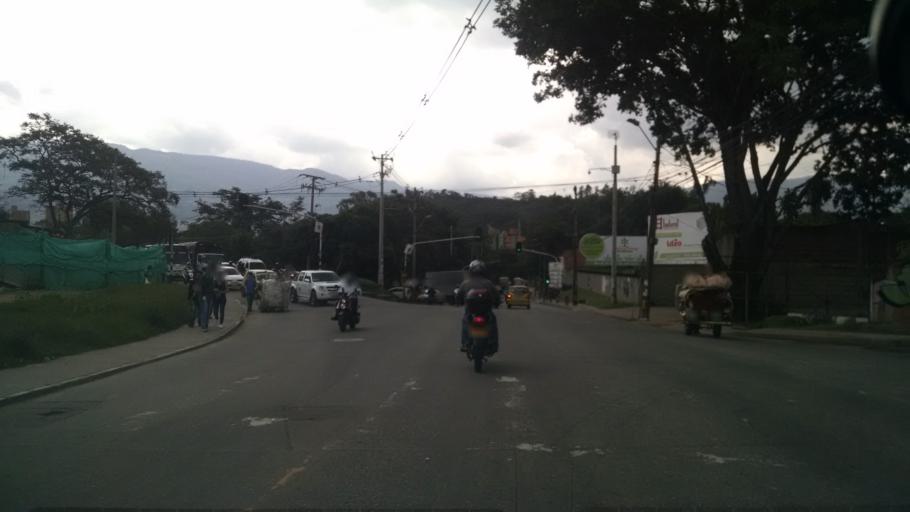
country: CO
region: Antioquia
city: Medellin
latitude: 6.2725
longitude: -75.5912
